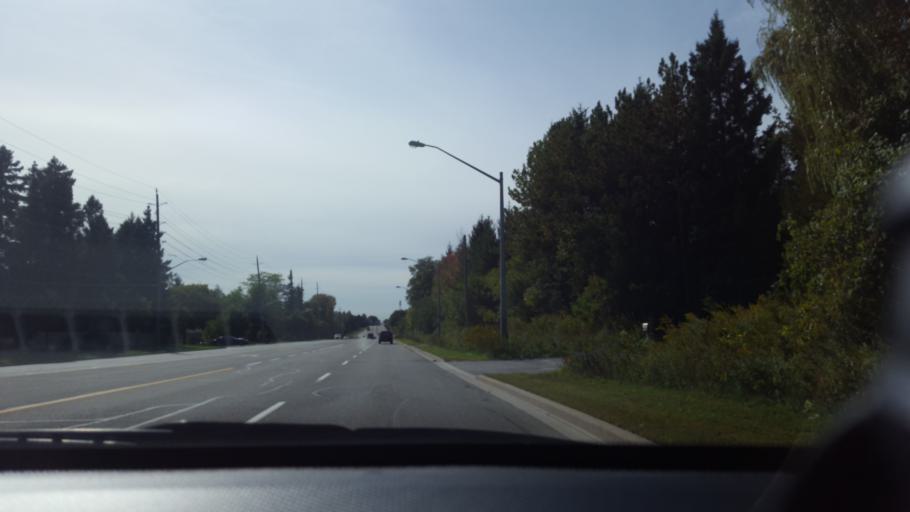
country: CA
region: Ontario
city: Newmarket
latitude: 43.9989
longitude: -79.4956
